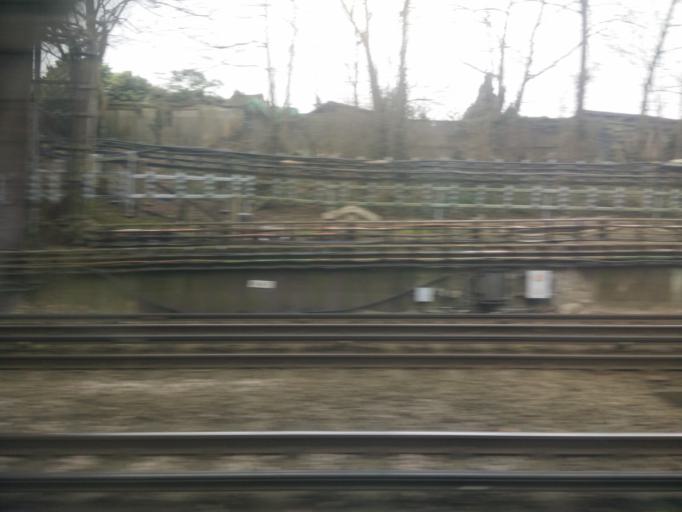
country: GB
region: England
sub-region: Greater London
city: Ruislip
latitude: 51.6067
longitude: -0.4209
